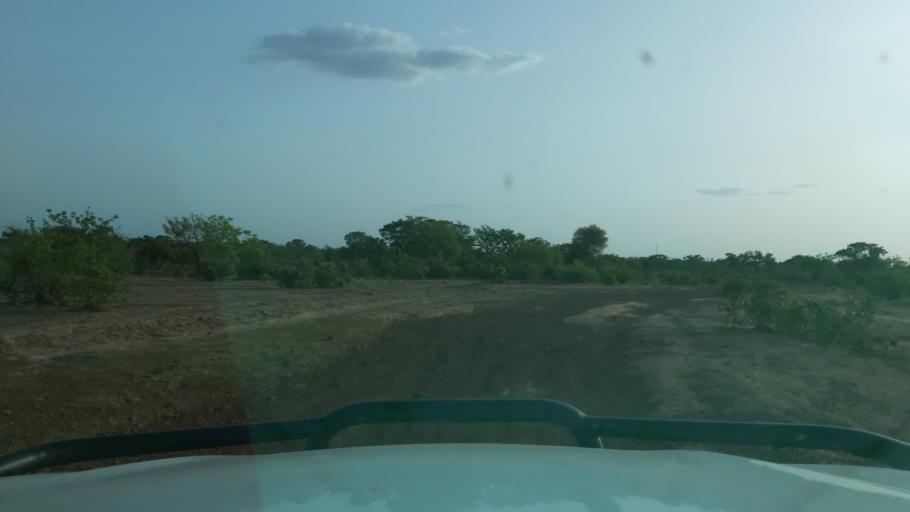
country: ML
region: Koulikoro
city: Kolokani
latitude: 13.2075
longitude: -7.9126
